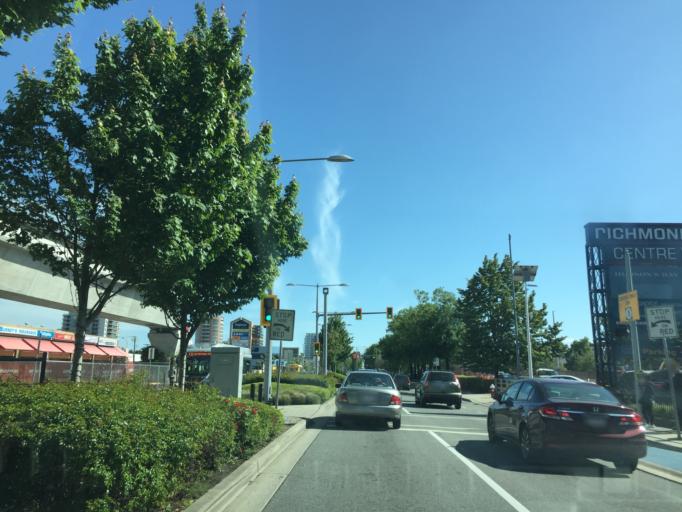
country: CA
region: British Columbia
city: Richmond
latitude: 49.1680
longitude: -123.1367
